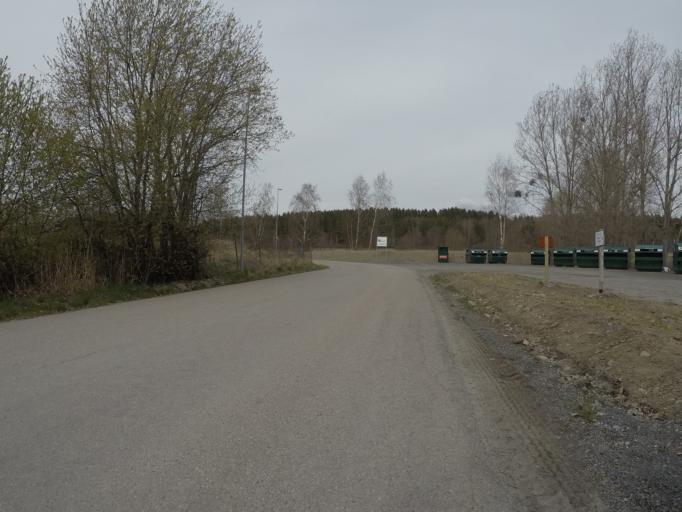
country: SE
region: Soedermanland
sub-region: Eskilstuna Kommun
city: Torshalla
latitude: 59.4227
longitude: 16.4879
